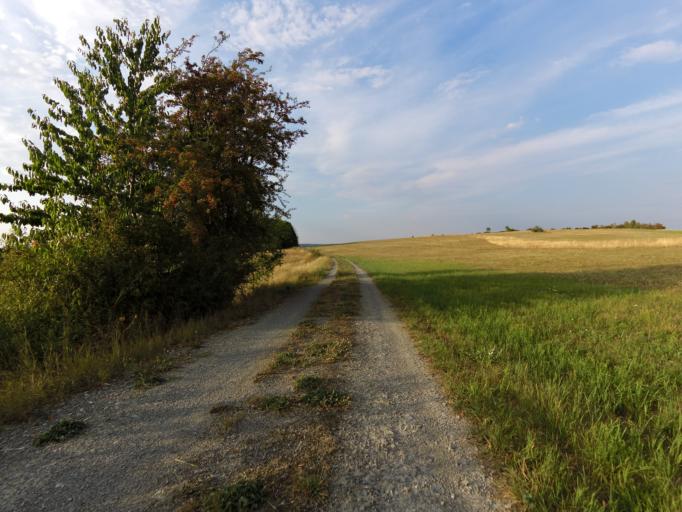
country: DE
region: Bavaria
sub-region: Regierungsbezirk Unterfranken
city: Zell am Main
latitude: 49.8003
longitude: 9.8677
